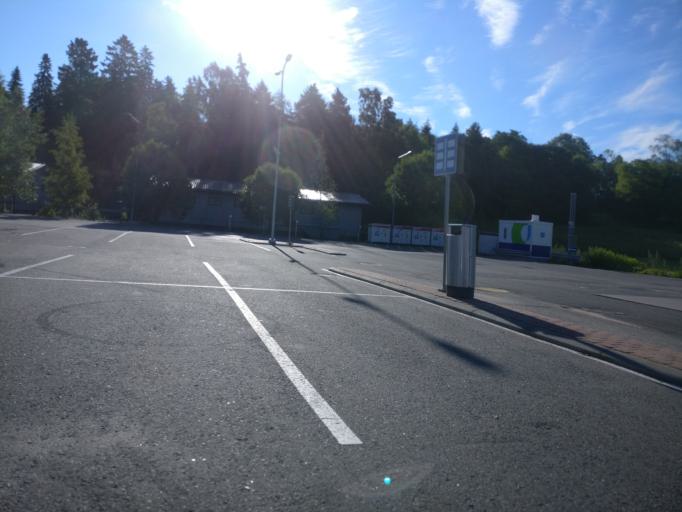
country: FI
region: Varsinais-Suomi
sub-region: Salo
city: Pernioe
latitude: 60.2044
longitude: 23.1131
